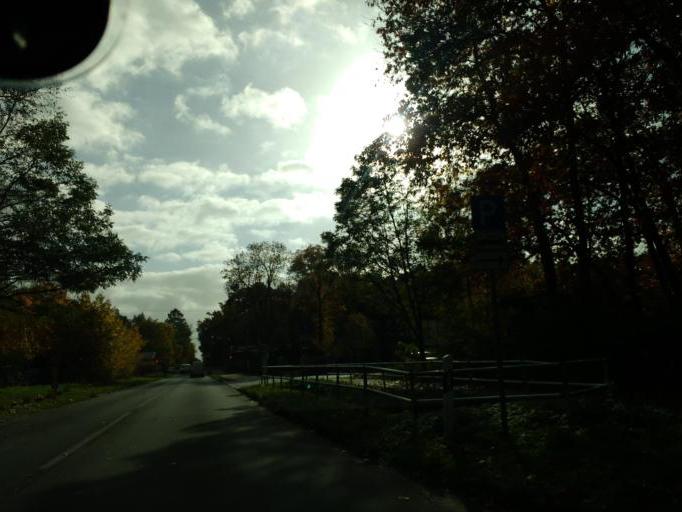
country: DE
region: Brandenburg
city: Grunheide
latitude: 52.4077
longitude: 13.8250
